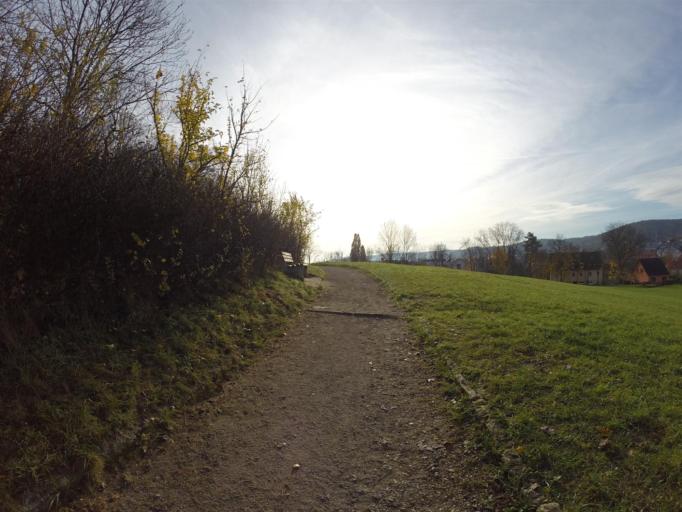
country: DE
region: Thuringia
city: Jena
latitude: 50.9272
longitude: 11.5718
